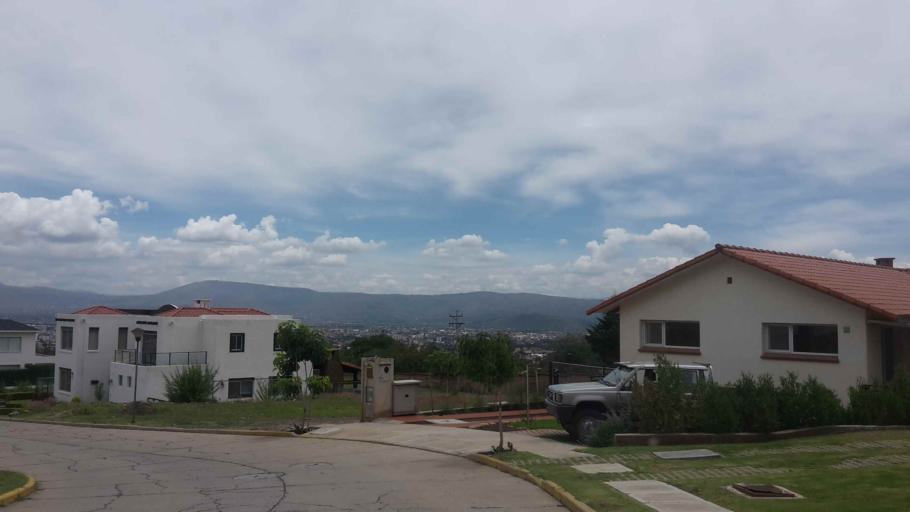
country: BO
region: Cochabamba
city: Cochabamba
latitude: -17.3397
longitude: -66.1875
